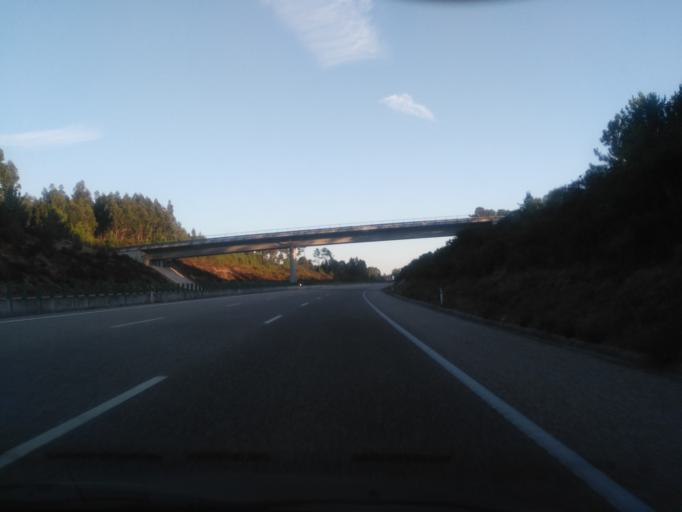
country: PT
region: Leiria
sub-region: Pombal
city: Lourical
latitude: 39.9784
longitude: -8.7835
